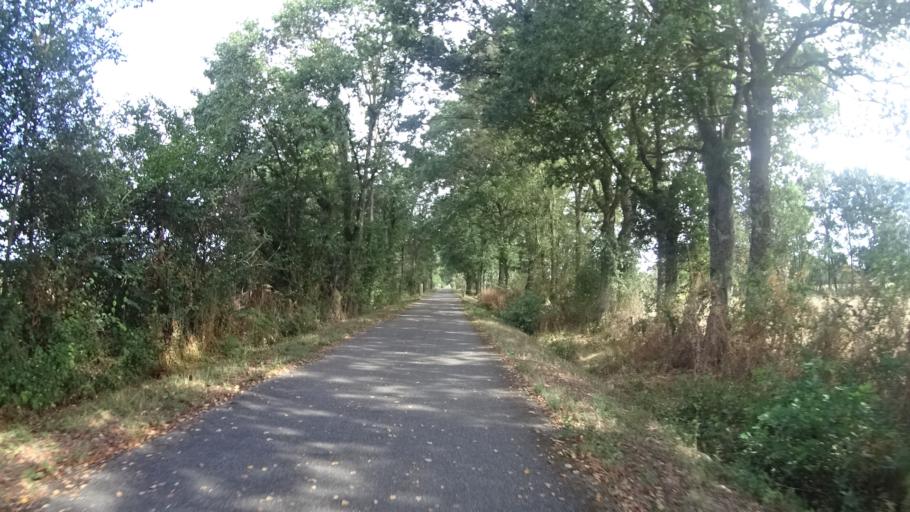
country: FR
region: Bourgogne
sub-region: Departement de Saone-et-Loire
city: Bourbon-Lancy
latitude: 46.5916
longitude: 3.7456
